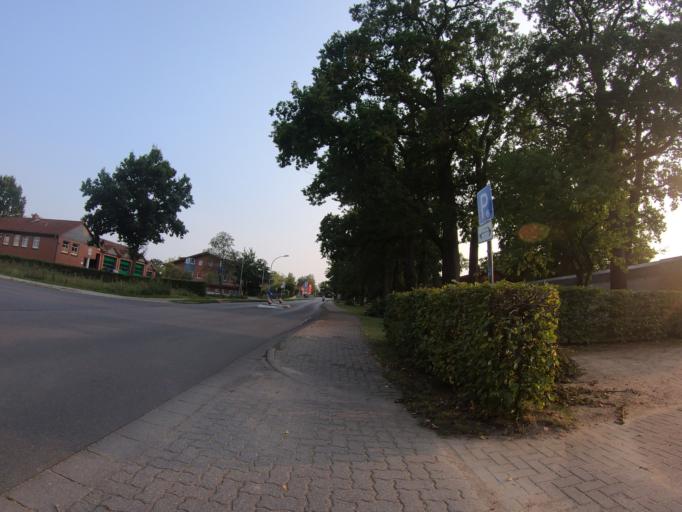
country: DE
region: Lower Saxony
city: Leiferde
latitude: 52.4424
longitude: 10.4356
